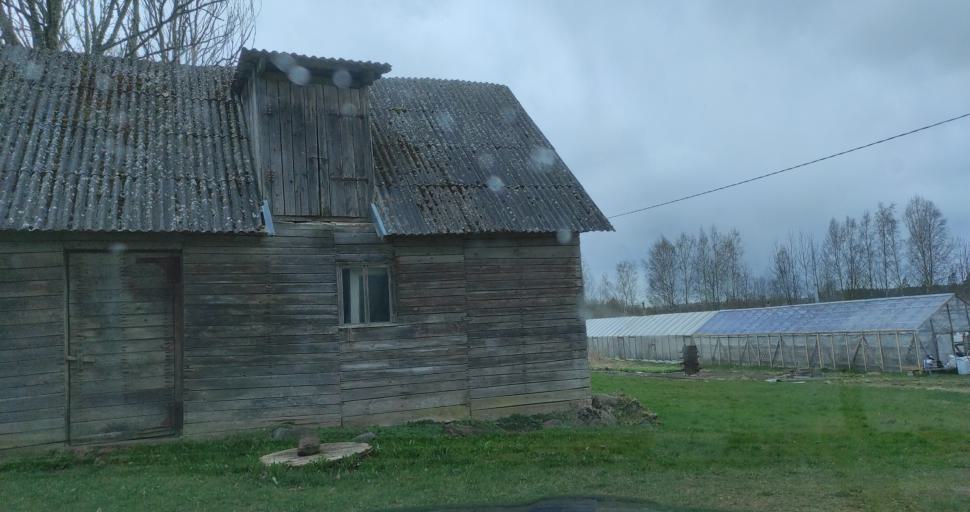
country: LV
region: Ventspils Rajons
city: Piltene
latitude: 57.0576
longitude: 21.7656
